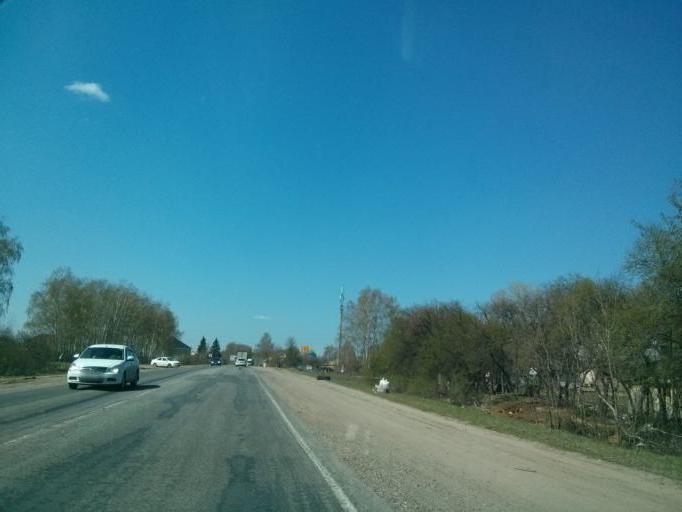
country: RU
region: Nizjnij Novgorod
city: Nizhniy Novgorod
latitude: 56.2112
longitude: 43.9734
